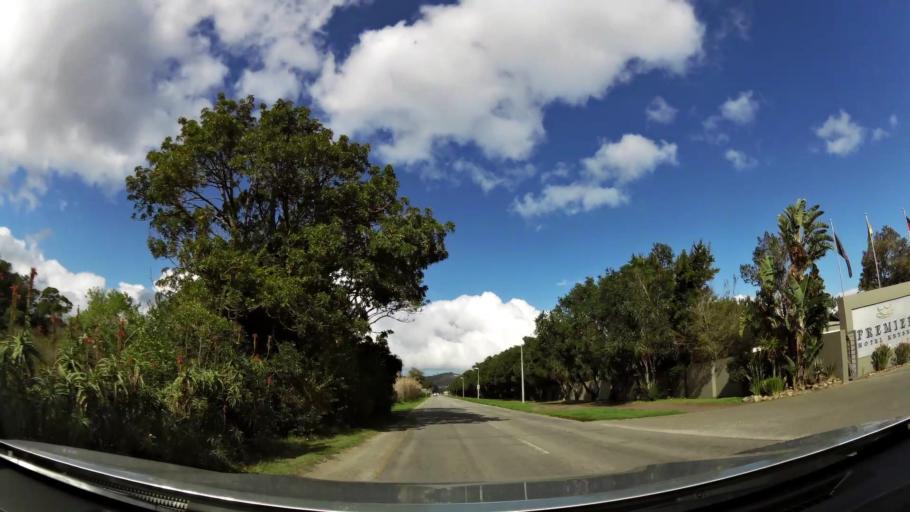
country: ZA
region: Western Cape
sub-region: Eden District Municipality
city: Knysna
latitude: -34.0505
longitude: 23.0699
